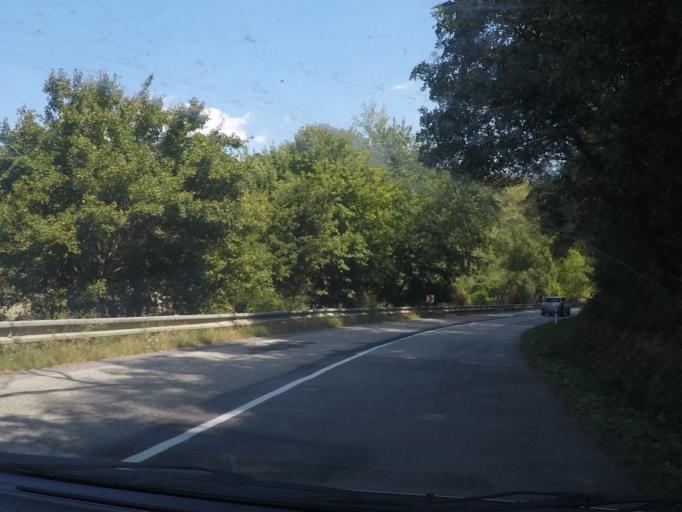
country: SK
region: Nitriansky
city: Tlmace
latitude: 48.2823
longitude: 18.4947
